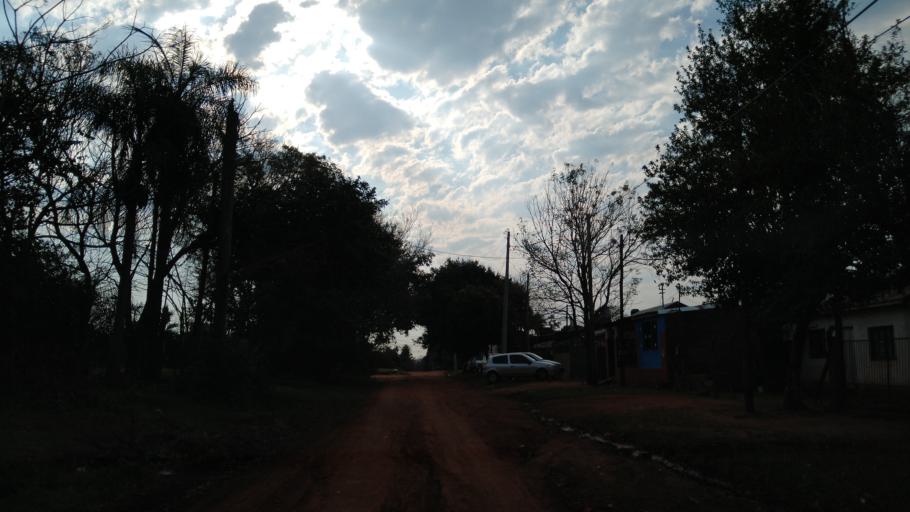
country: AR
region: Misiones
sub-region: Departamento de Capital
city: Posadas
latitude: -27.4286
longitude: -55.8768
